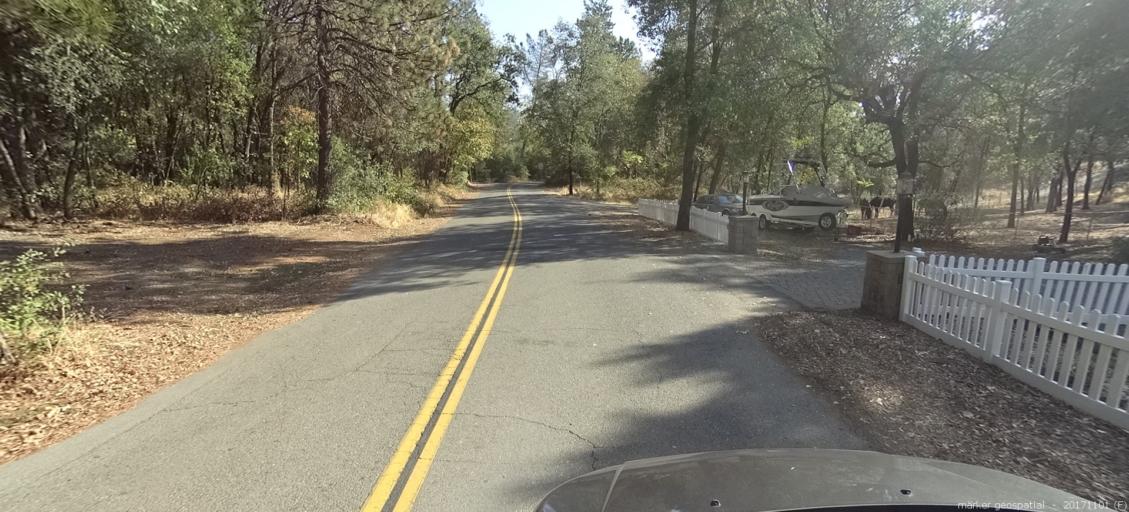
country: US
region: California
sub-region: Shasta County
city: Central Valley (historical)
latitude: 40.6766
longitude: -122.4071
